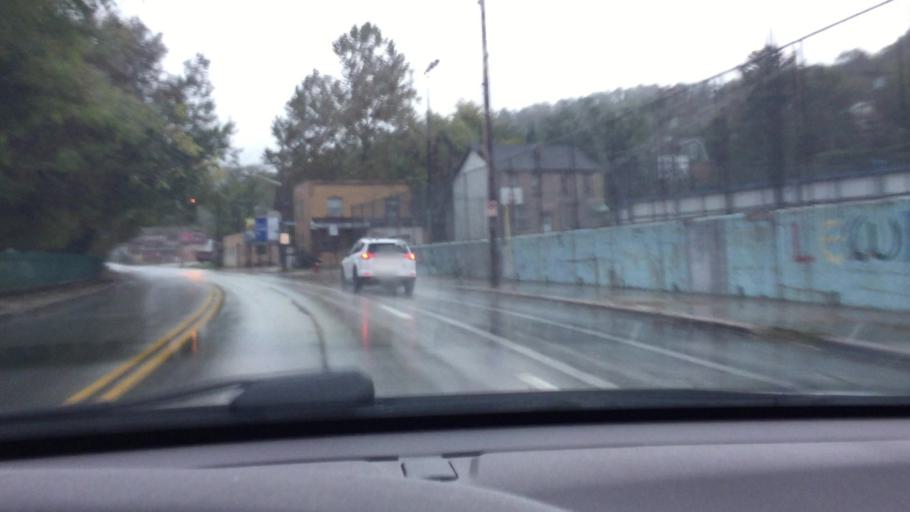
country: US
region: Pennsylvania
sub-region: Allegheny County
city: Homestead
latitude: 40.4127
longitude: -79.9451
